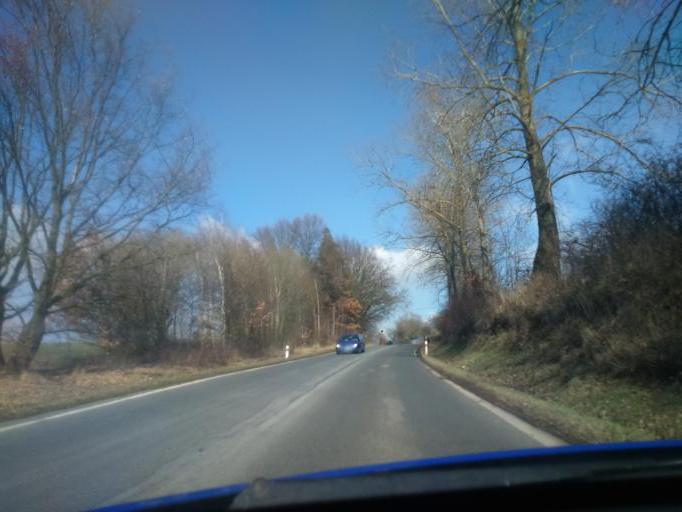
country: CZ
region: Plzensky
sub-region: Okres Domazlice
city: Domazlice
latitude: 49.4502
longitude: 12.9349
